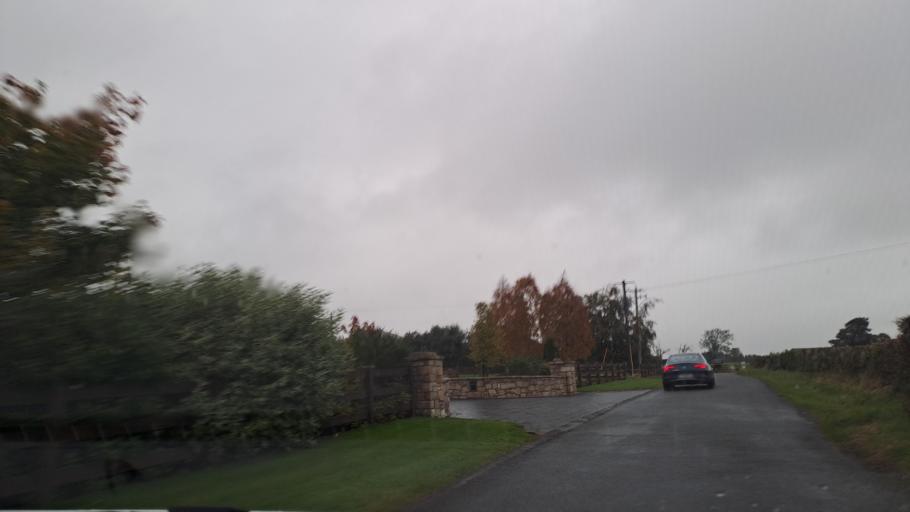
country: IE
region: Ulster
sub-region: County Monaghan
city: Monaghan
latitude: 54.2104
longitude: -6.9090
